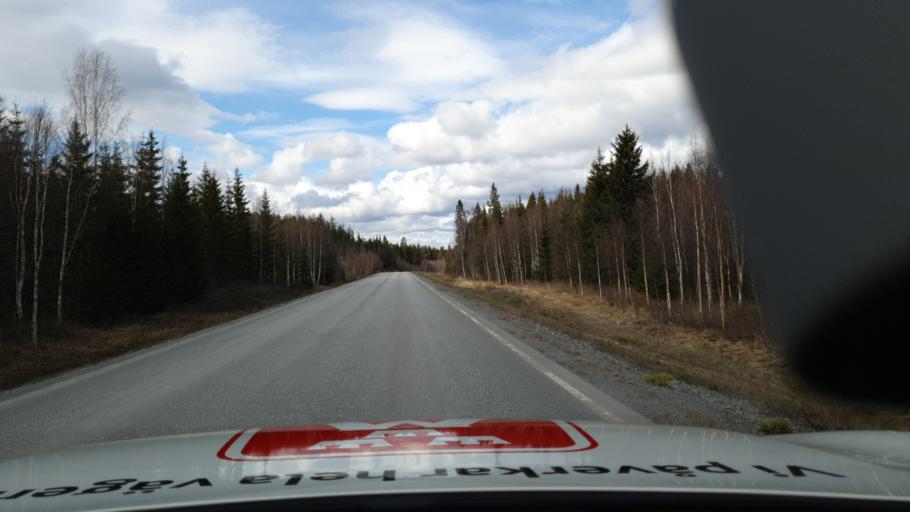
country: SE
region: Jaemtland
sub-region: Krokoms Kommun
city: Krokom
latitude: 63.3186
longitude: 14.4250
